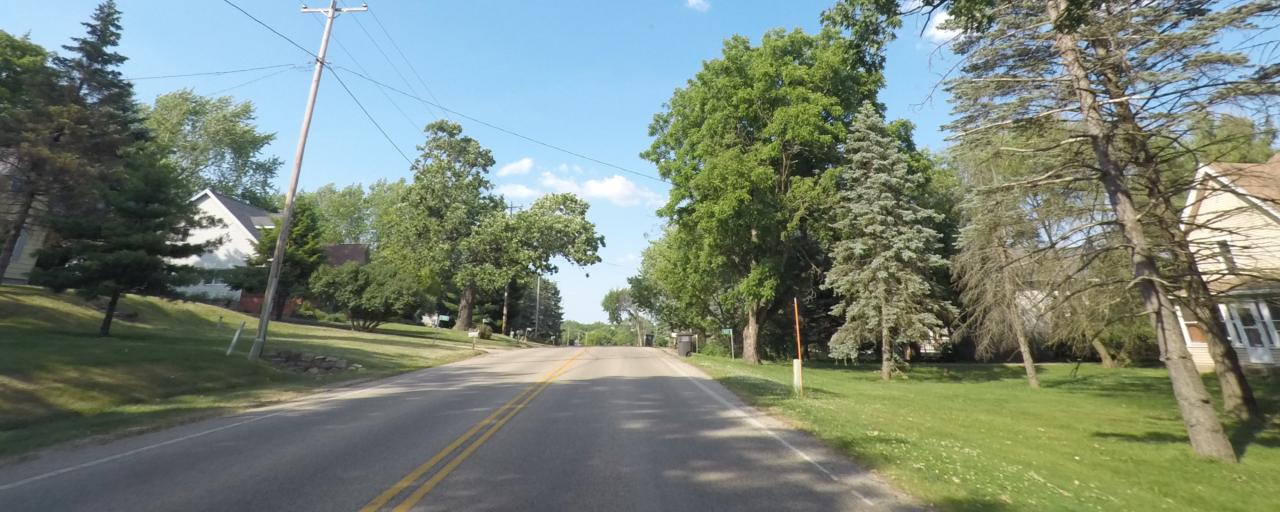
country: US
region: Wisconsin
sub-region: Walworth County
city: Potter Lake
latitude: 42.8230
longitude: -88.3201
